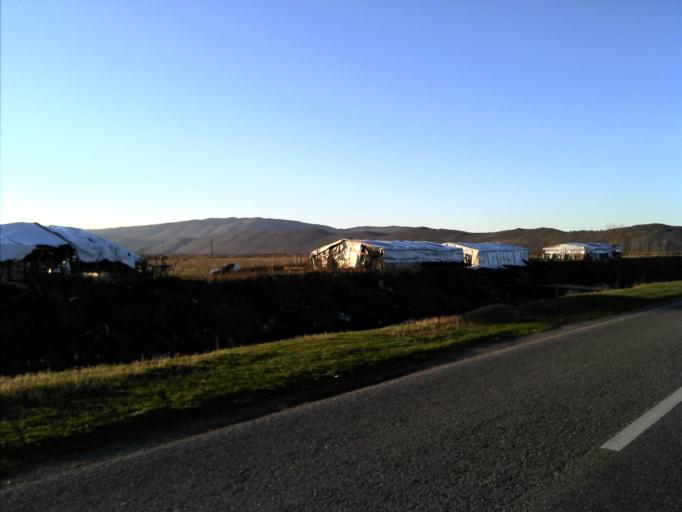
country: AL
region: Shkoder
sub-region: Rrethi i Shkodres
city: Dajc
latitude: 41.9505
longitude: 19.4531
